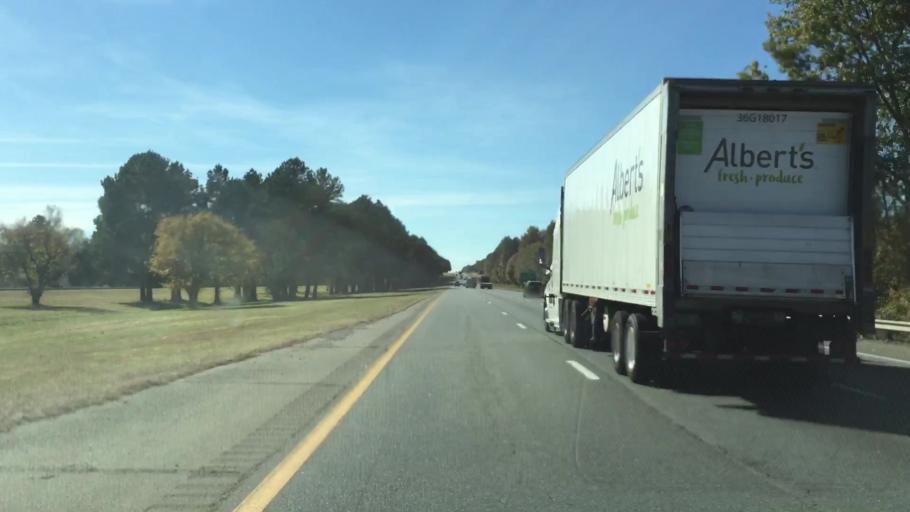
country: US
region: North Carolina
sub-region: Davidson County
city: Lexington
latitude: 35.7871
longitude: -80.2363
